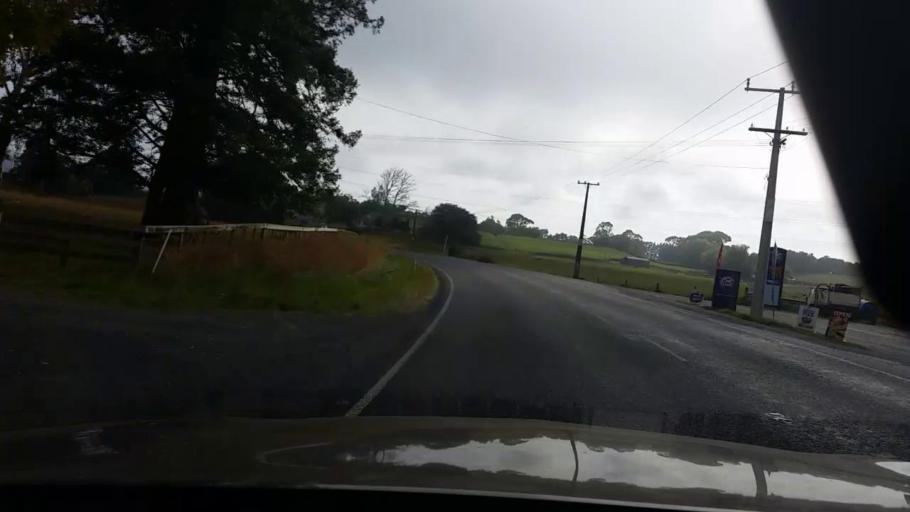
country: NZ
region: Waikato
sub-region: Hamilton City
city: Hamilton
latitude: -37.6195
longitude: 175.3372
